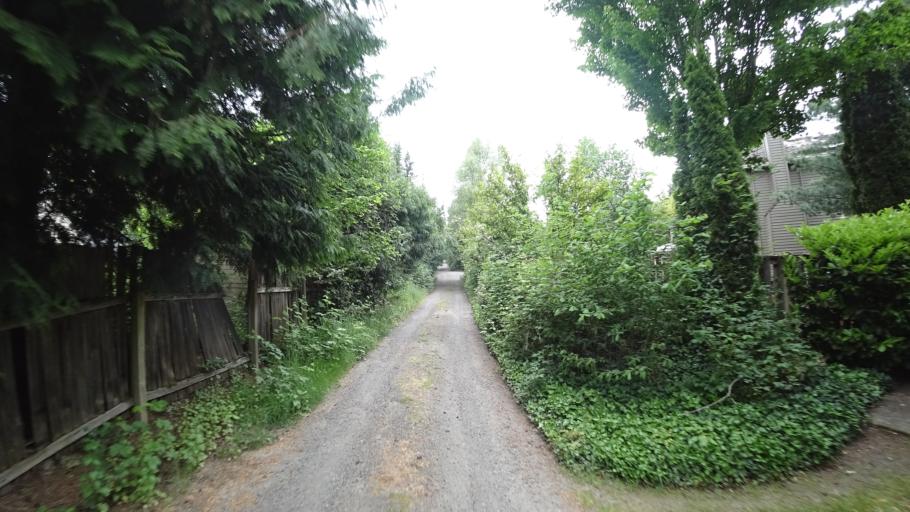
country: US
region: Oregon
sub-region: Washington County
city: Garden Home-Whitford
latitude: 45.4639
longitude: -122.7437
